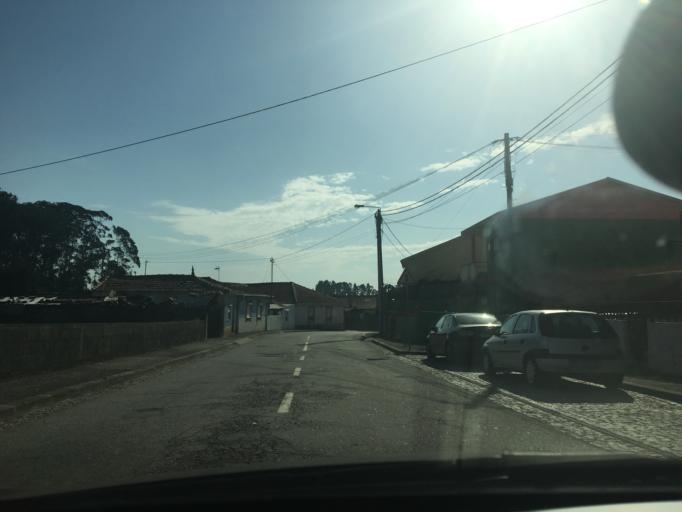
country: PT
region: Porto
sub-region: Maia
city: Gemunde
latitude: 41.2519
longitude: -8.6409
